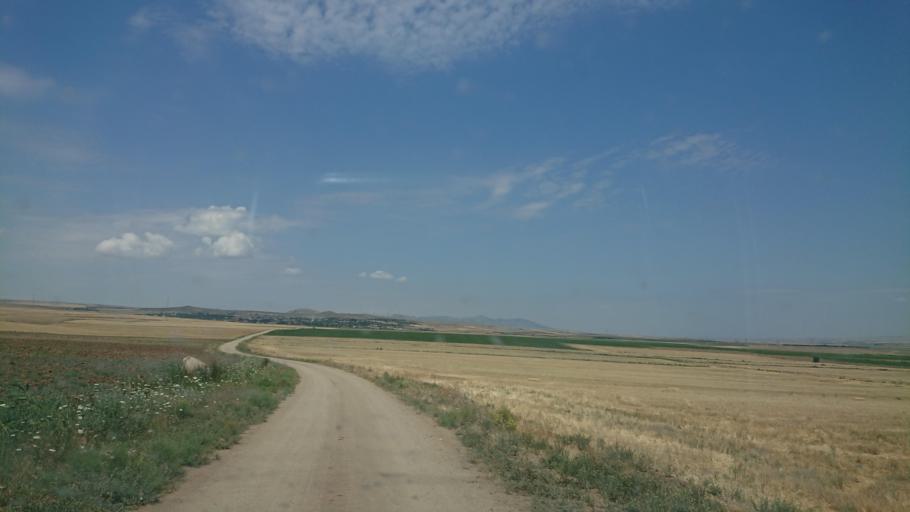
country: TR
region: Aksaray
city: Agacoren
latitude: 38.9559
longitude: 33.9217
